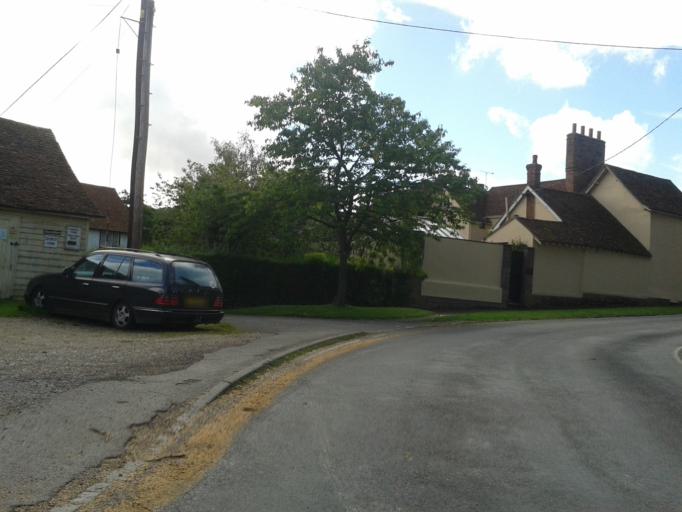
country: GB
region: England
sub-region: Cambridgeshire
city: Duxford
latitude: 52.0359
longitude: 0.1308
